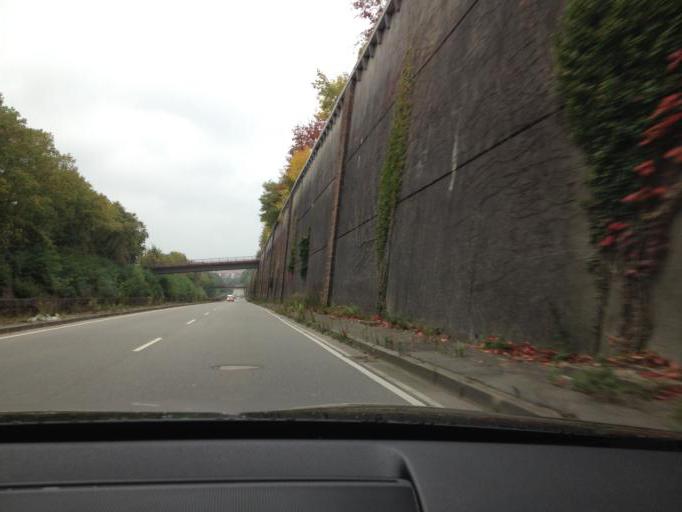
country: DE
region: Rheinland-Pfalz
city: Zweibrucken
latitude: 49.2452
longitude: 7.3726
